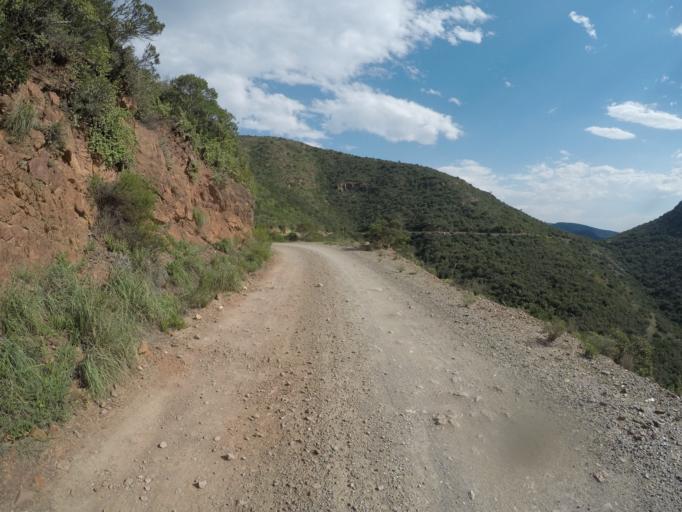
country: ZA
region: Eastern Cape
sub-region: Cacadu District Municipality
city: Kareedouw
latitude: -33.6479
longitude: 24.3446
